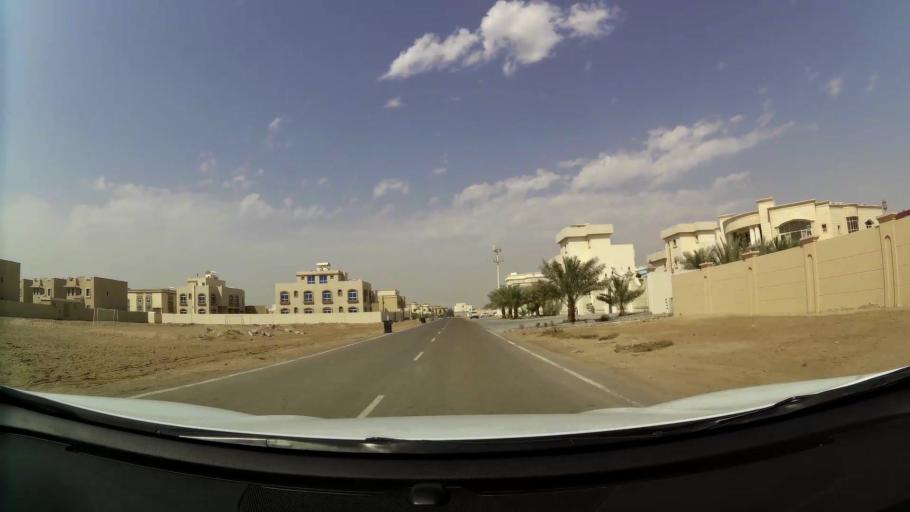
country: AE
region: Abu Dhabi
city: Abu Dhabi
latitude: 24.3280
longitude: 54.5461
